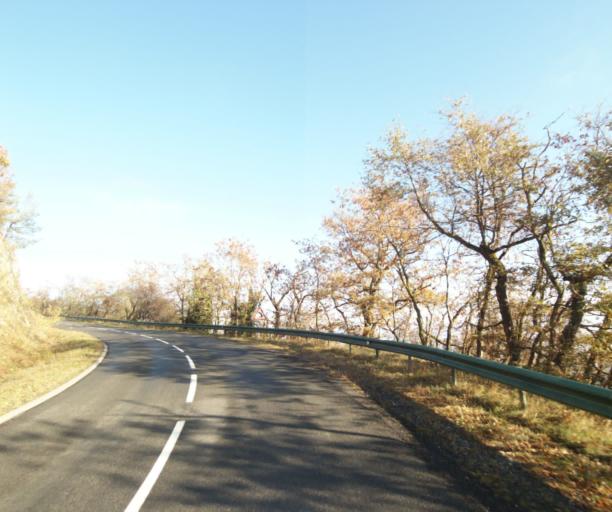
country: FR
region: Auvergne
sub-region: Departement du Puy-de-Dome
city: Nohanent
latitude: 45.8107
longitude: 3.0445
